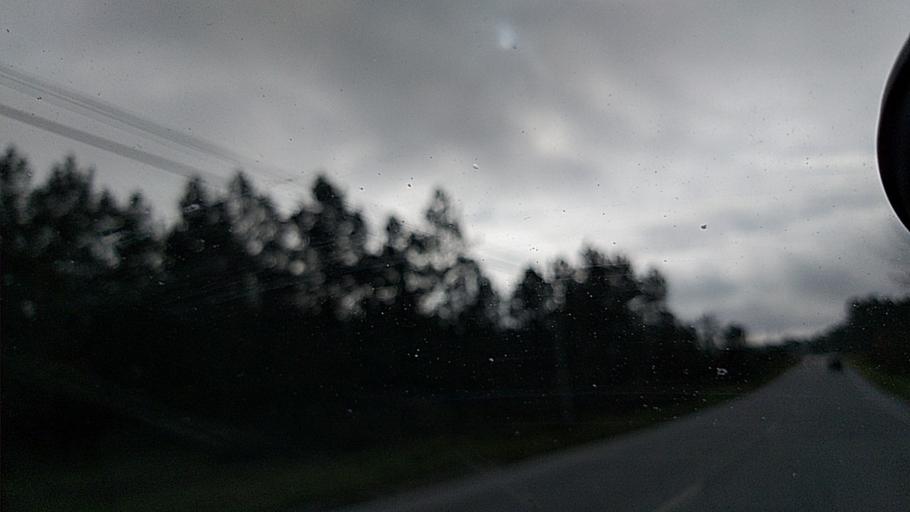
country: PT
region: Guarda
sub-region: Aguiar da Beira
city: Aguiar da Beira
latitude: 40.8112
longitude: -7.5343
